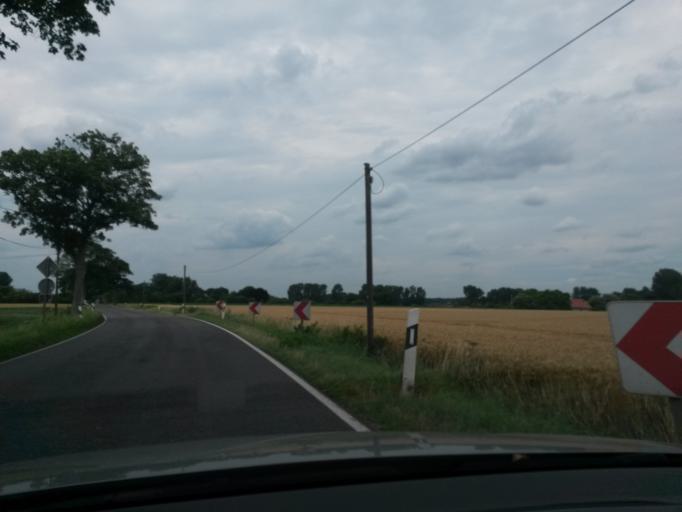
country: DE
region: North Rhine-Westphalia
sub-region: Regierungsbezirk Dusseldorf
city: Viersen
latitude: 51.3004
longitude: 6.3881
